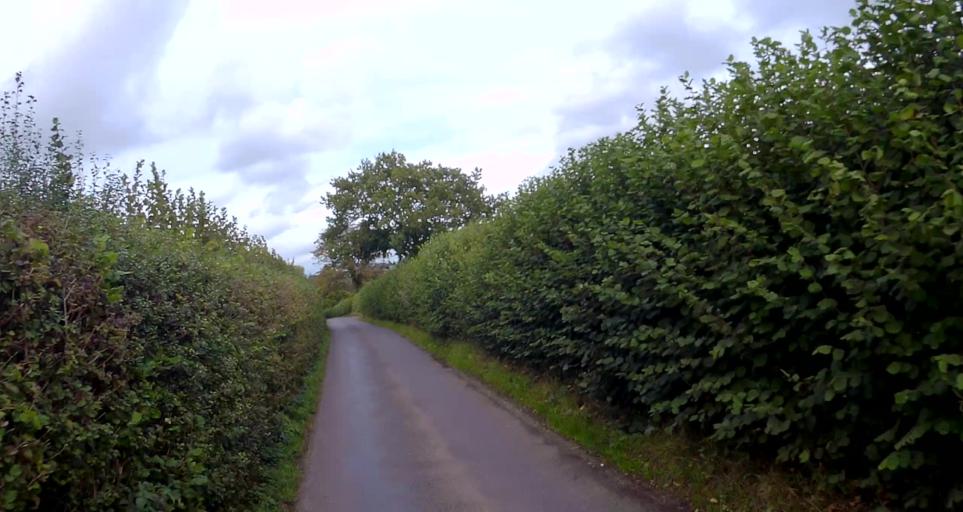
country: GB
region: England
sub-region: Hampshire
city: Four Marks
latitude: 51.1180
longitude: -1.0949
